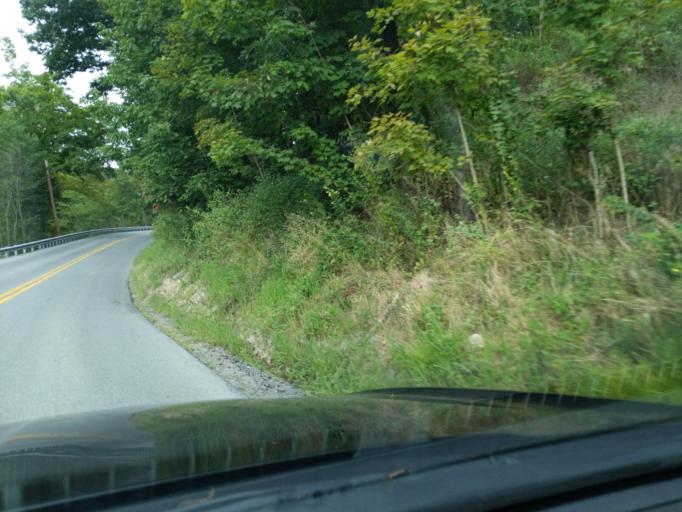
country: US
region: Pennsylvania
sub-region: Blair County
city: Claysburg
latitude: 40.3568
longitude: -78.4732
